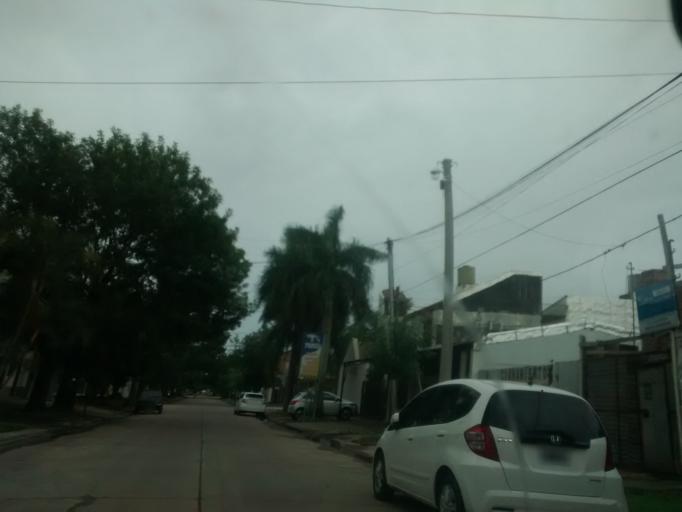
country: AR
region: Chaco
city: Resistencia
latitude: -27.4431
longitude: -58.9844
